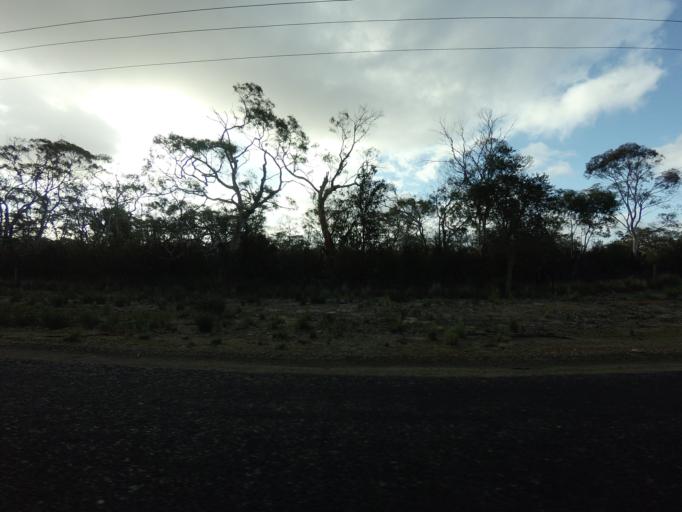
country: AU
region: Tasmania
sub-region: Break O'Day
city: St Helens
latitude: -42.0920
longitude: 148.1073
